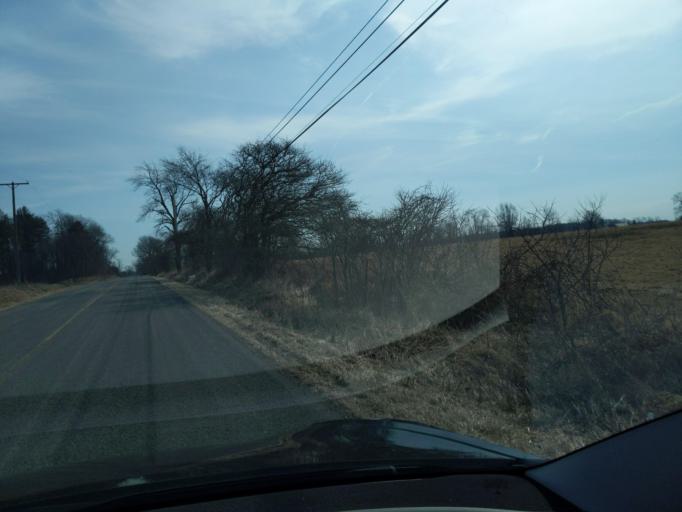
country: US
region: Michigan
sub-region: Ingham County
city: Williamston
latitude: 42.6585
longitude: -84.3337
